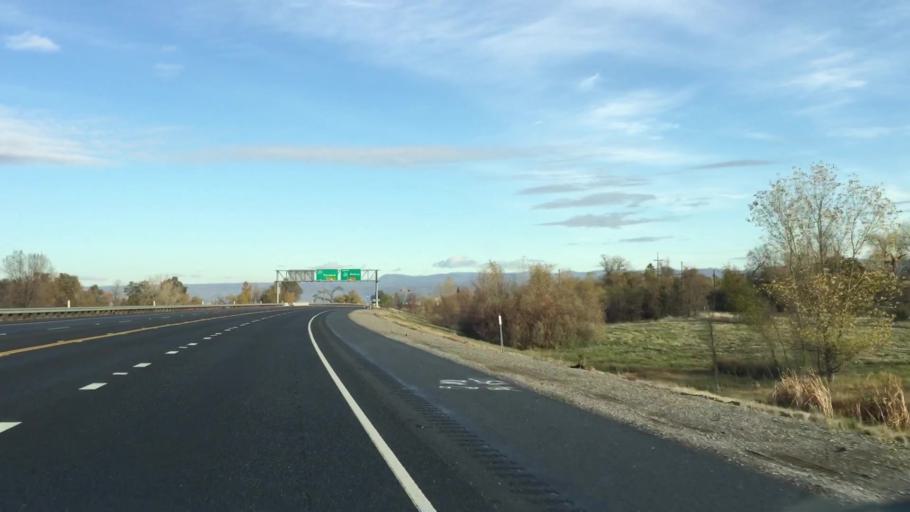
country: US
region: California
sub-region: Butte County
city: Thermalito
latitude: 39.5974
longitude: -121.6206
